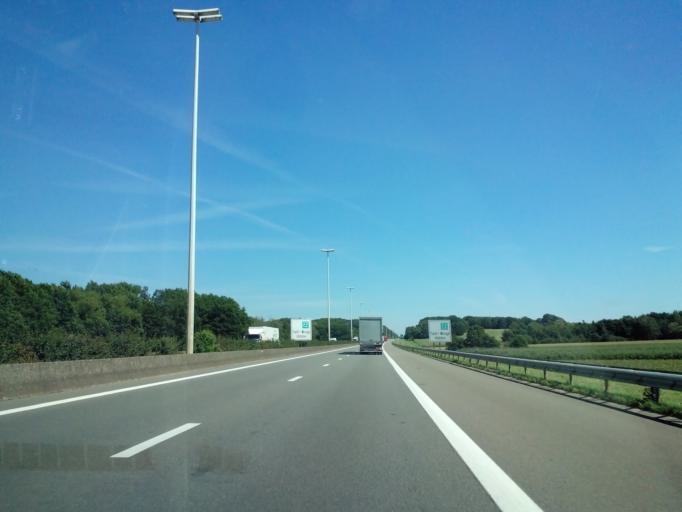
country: BE
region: Flanders
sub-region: Provincie Vlaams-Brabant
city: Bekkevoort
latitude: 50.9597
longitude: 4.9039
